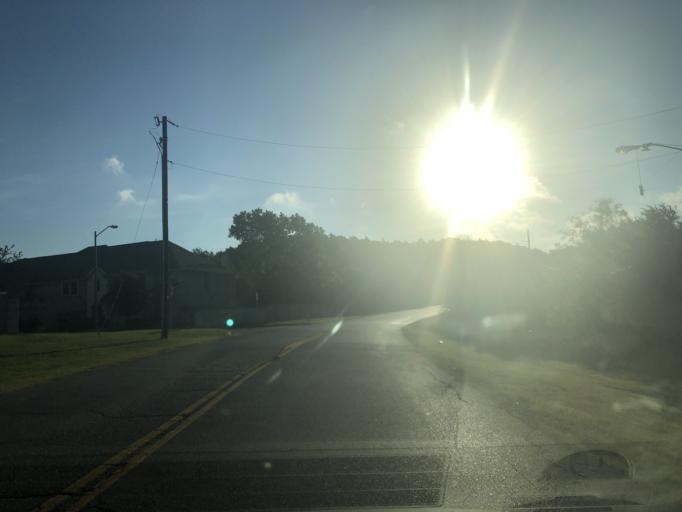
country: US
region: Texas
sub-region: Dallas County
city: Duncanville
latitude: 32.6653
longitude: -96.9593
